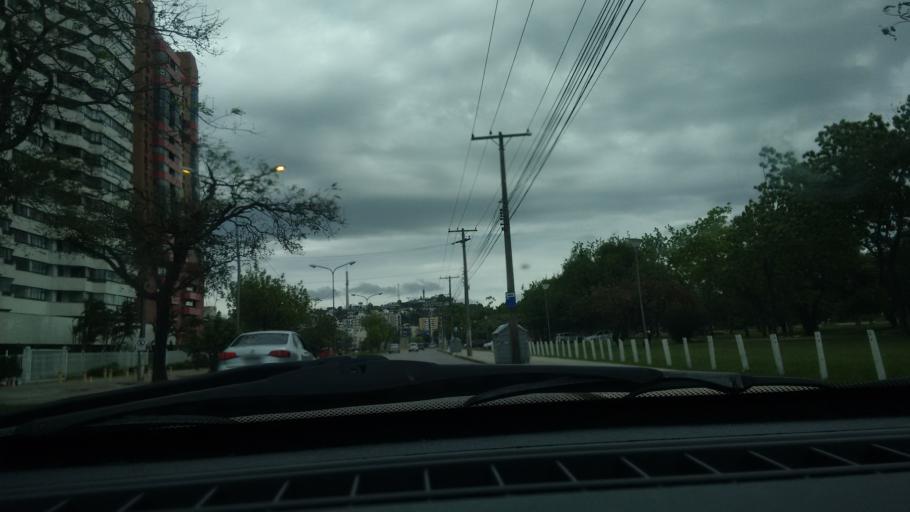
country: BR
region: Rio Grande do Sul
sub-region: Porto Alegre
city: Porto Alegre
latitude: -30.0548
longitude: -51.2303
